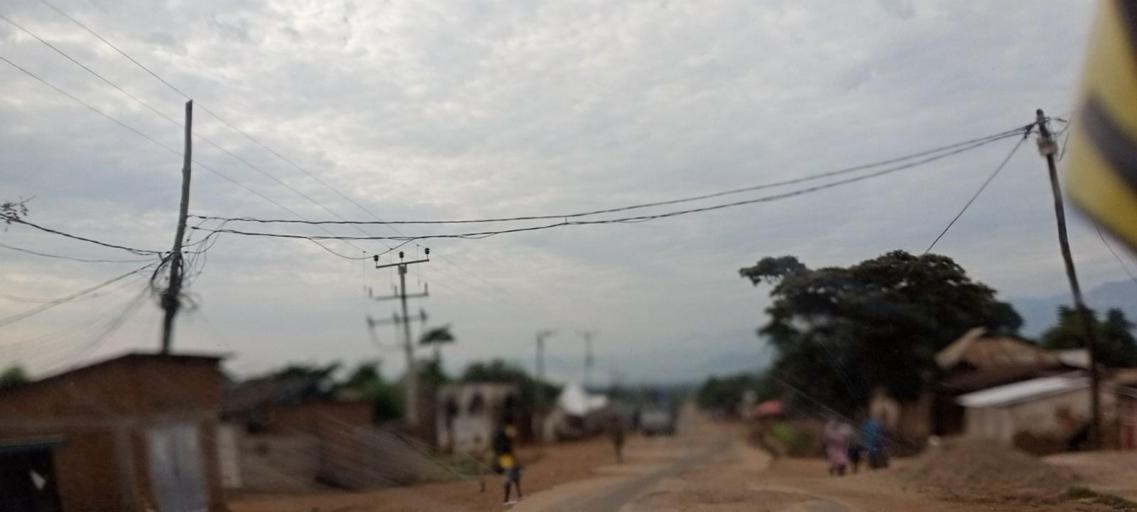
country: BI
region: Cibitoke
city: Cibitoke
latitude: -2.7399
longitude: 29.0027
